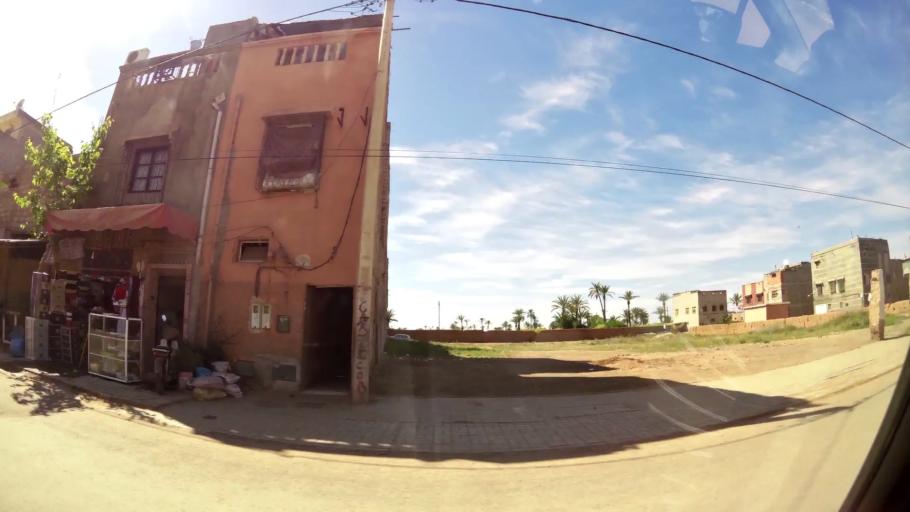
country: MA
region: Marrakech-Tensift-Al Haouz
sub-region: Marrakech
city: Marrakesh
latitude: 31.6288
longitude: -7.9594
